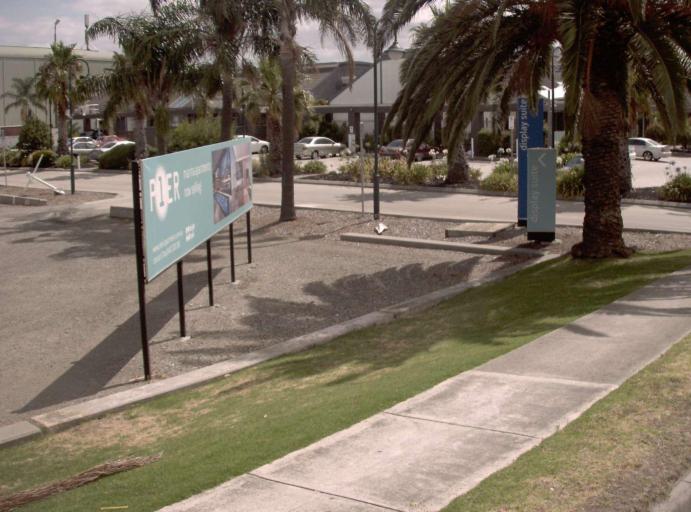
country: AU
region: Victoria
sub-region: Kingston
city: Patterson Lakes
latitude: -38.0714
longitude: 145.1360
